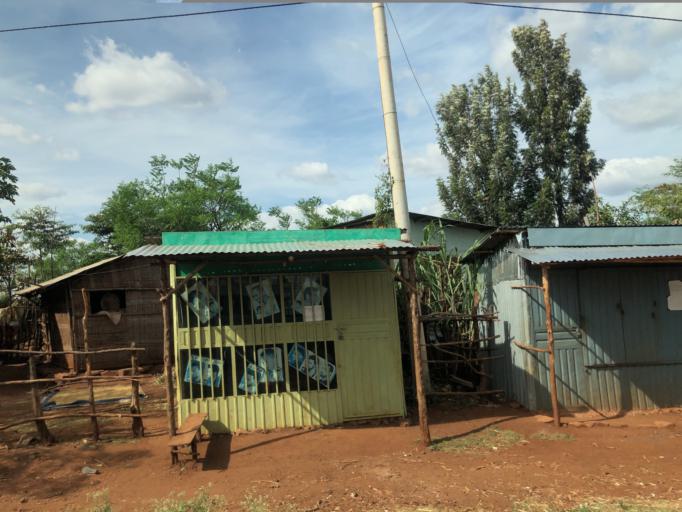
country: ET
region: Southern Nations, Nationalities, and People's Region
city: Konso
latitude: 5.3300
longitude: 37.4061
